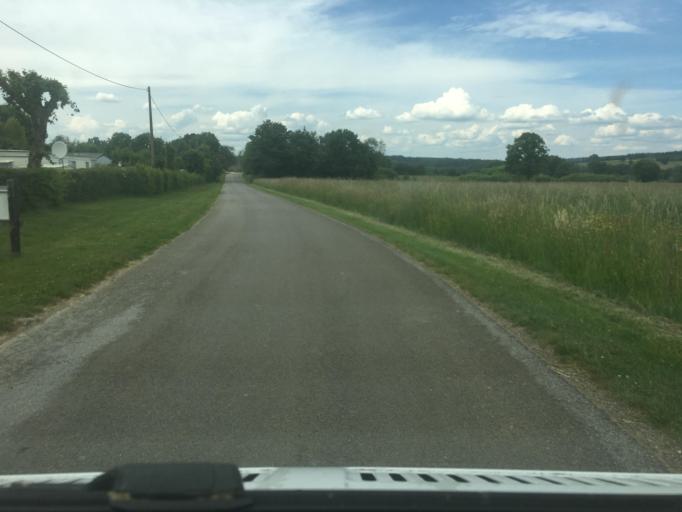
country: BE
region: Wallonia
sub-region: Province du Luxembourg
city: Florenville
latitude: 49.7114
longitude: 5.2616
